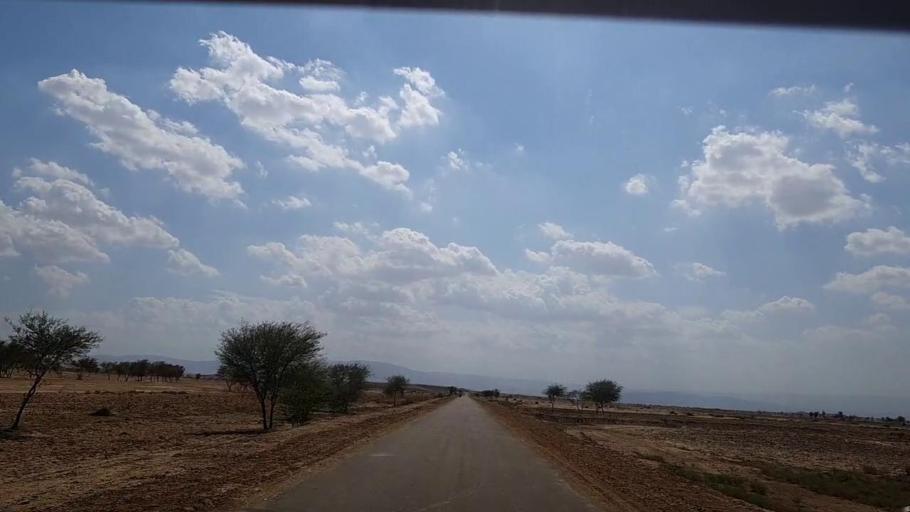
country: PK
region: Sindh
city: Johi
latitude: 26.5283
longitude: 67.5260
